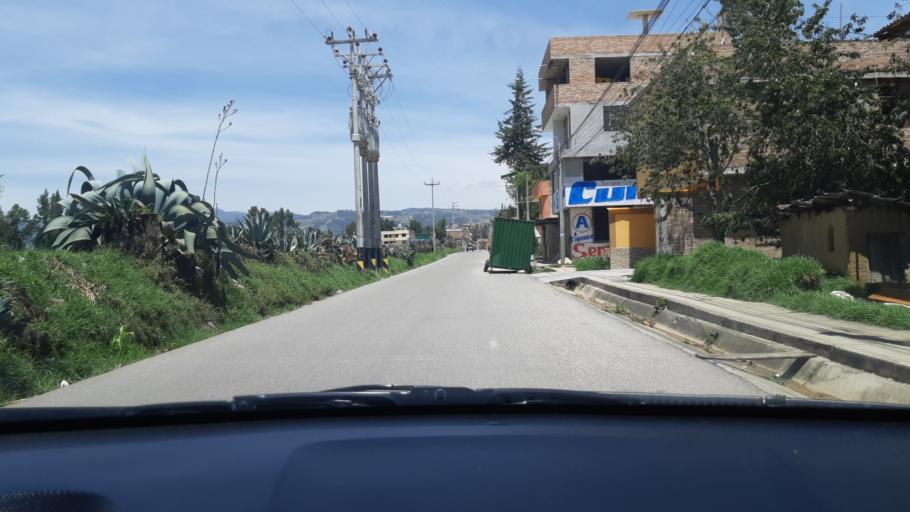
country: PE
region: Cajamarca
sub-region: Provincia de Cajamarca
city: Llacanora
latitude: -7.1720
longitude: -78.4578
